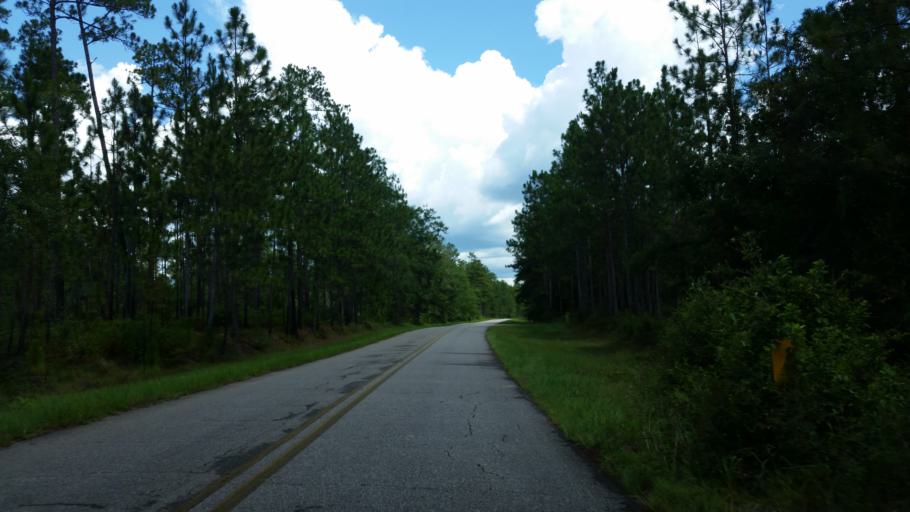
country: US
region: Florida
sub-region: Santa Rosa County
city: East Milton
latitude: 30.7421
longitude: -86.8266
